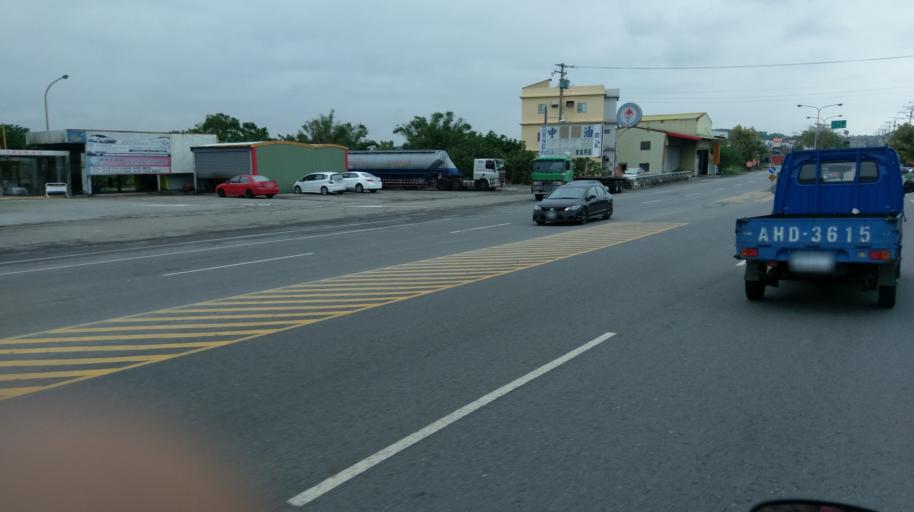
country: TW
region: Taiwan
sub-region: Miaoli
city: Miaoli
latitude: 24.6609
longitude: 120.8766
